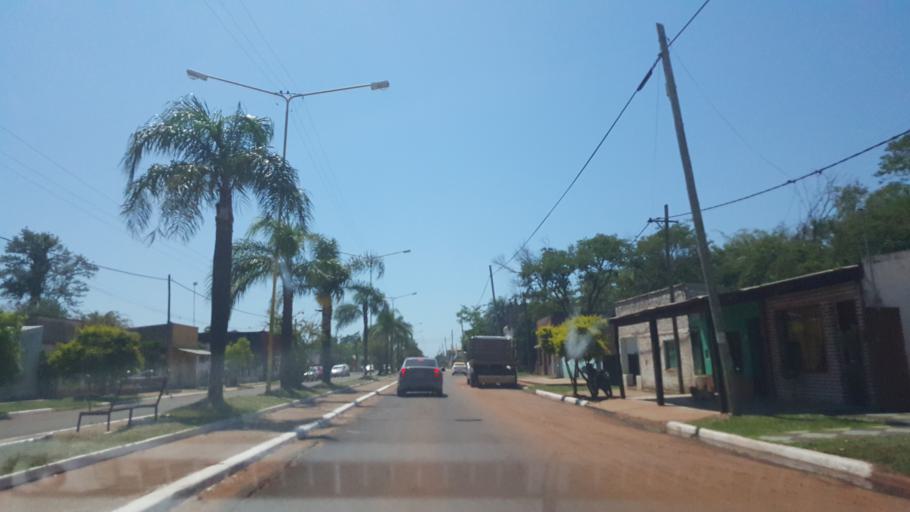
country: AR
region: Corrientes
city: Santo Tome
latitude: -28.5472
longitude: -56.0601
